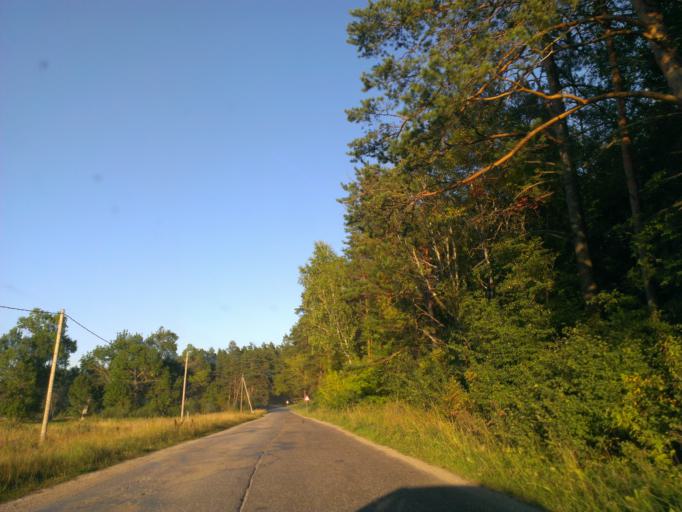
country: LV
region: Garkalne
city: Garkalne
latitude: 57.0654
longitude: 24.4088
